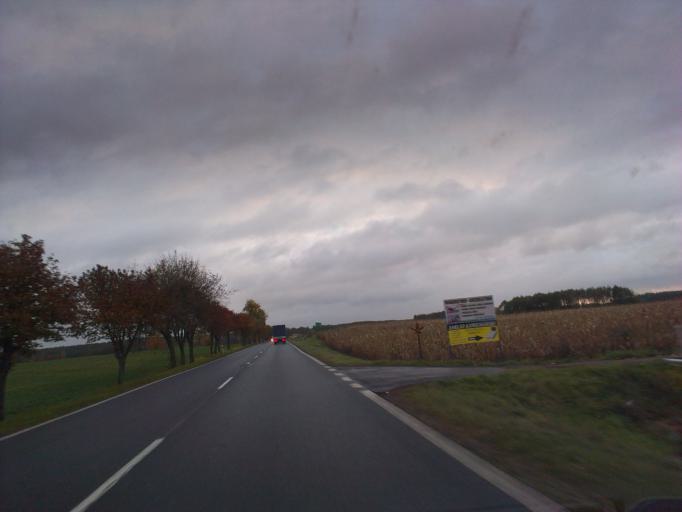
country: PL
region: Kujawsko-Pomorskie
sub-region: Powiat tucholski
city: Lubiewo
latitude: 53.5035
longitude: 18.0135
